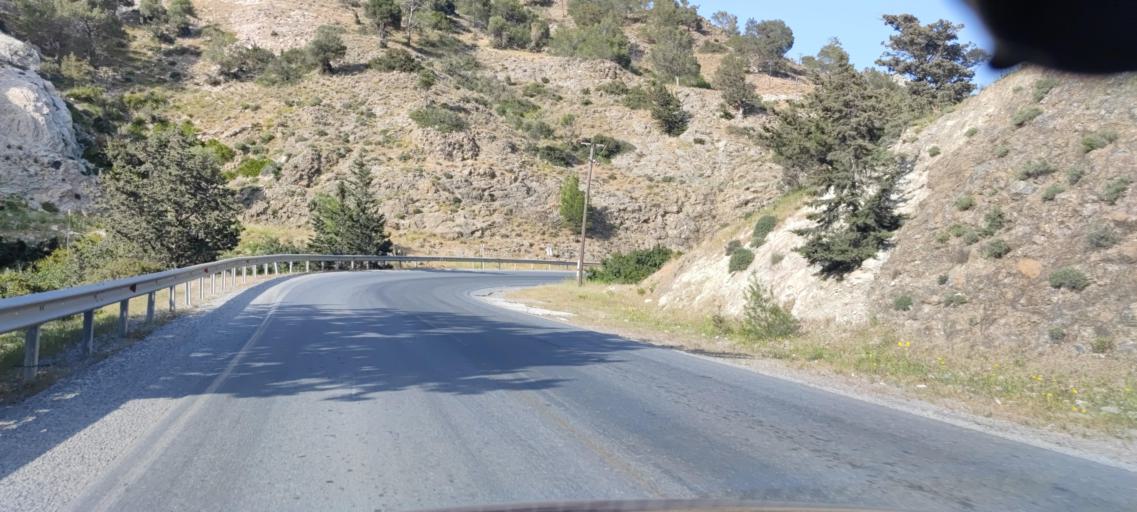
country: CY
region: Keryneia
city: Lapithos
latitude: 35.3392
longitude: 33.0703
